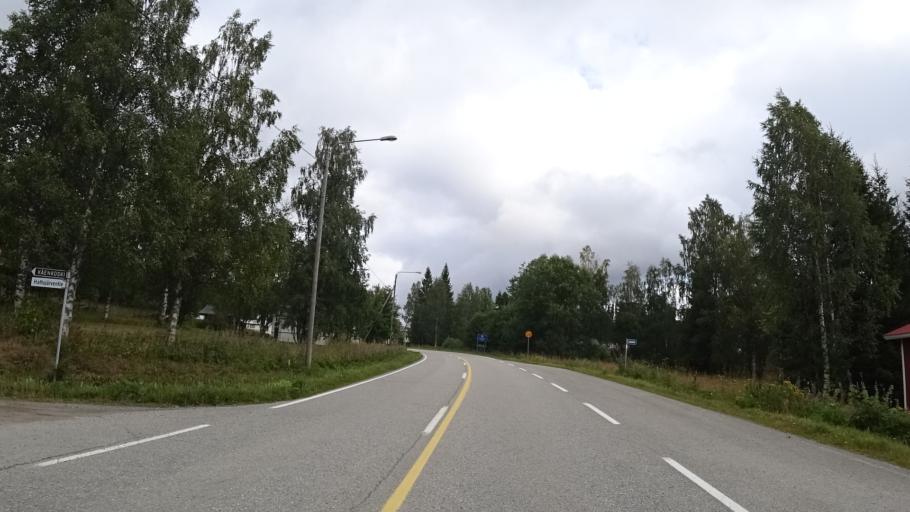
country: FI
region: North Karelia
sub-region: Joensuu
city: Ilomantsi
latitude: 62.9316
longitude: 31.2809
